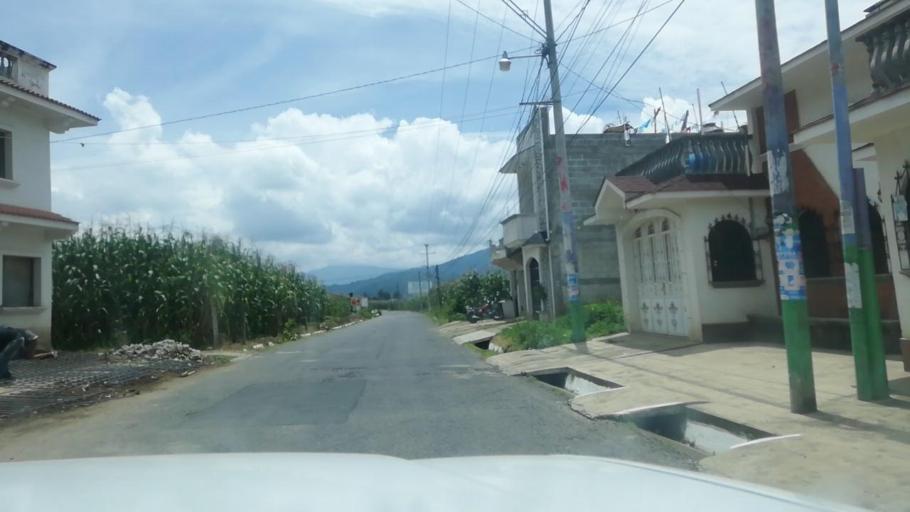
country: GT
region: Totonicapan
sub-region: Municipio de San Andres Xecul
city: San Andres Xecul
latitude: 14.9051
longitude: -91.4737
